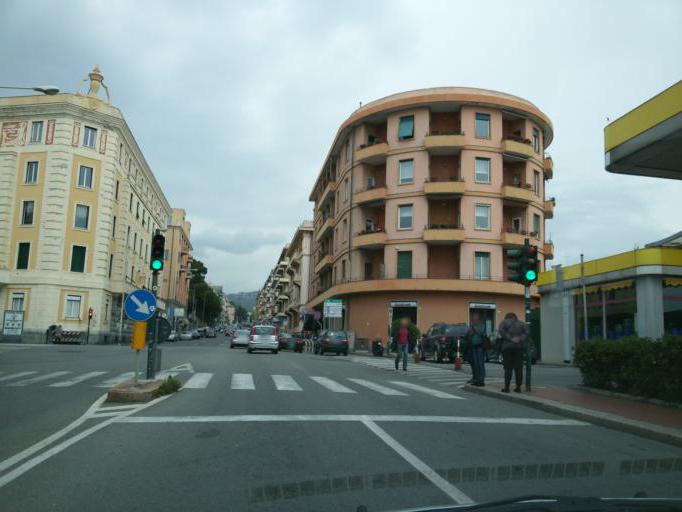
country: IT
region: Liguria
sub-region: Provincia di Genova
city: San Teodoro
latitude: 44.3908
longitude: 8.9742
